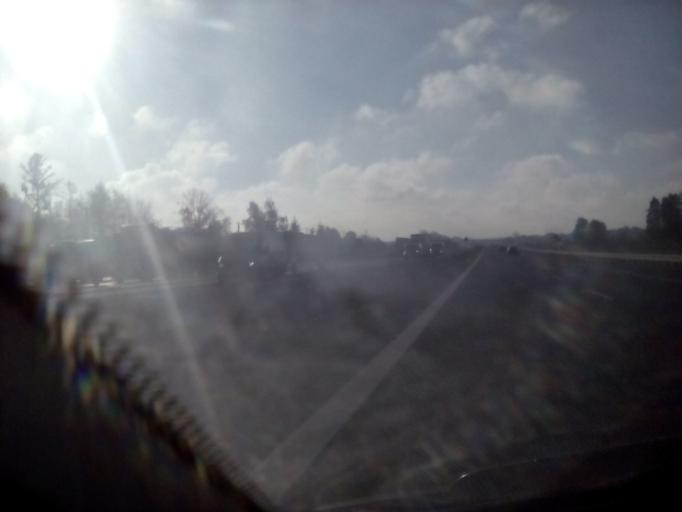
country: PL
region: Masovian Voivodeship
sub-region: Powiat grojecki
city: Grojec
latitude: 51.8108
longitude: 20.8854
